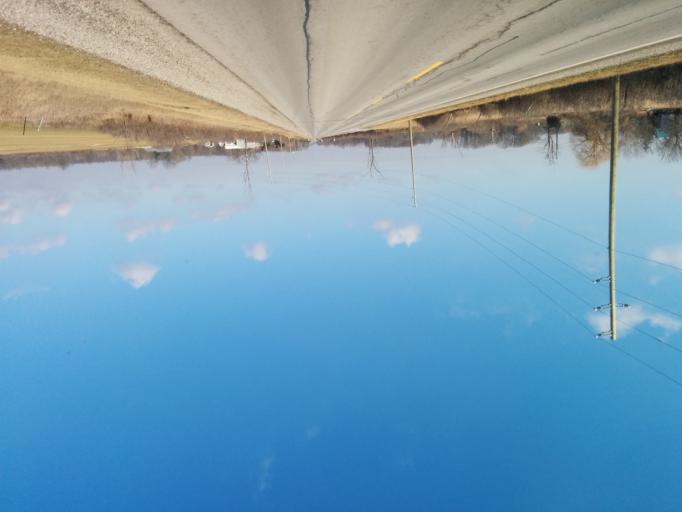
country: CA
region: Ontario
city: Brantford
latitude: 42.9947
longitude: -80.1407
